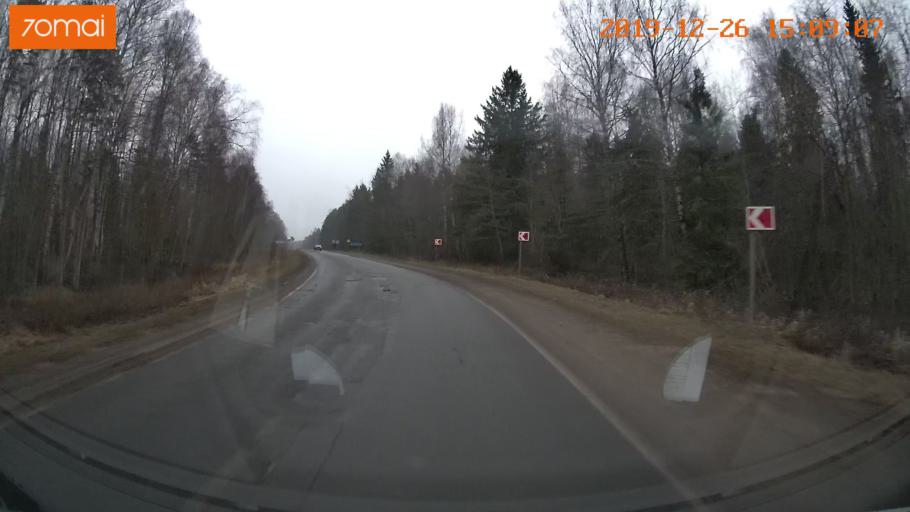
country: RU
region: Jaroslavl
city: Rybinsk
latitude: 58.1521
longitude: 38.8380
